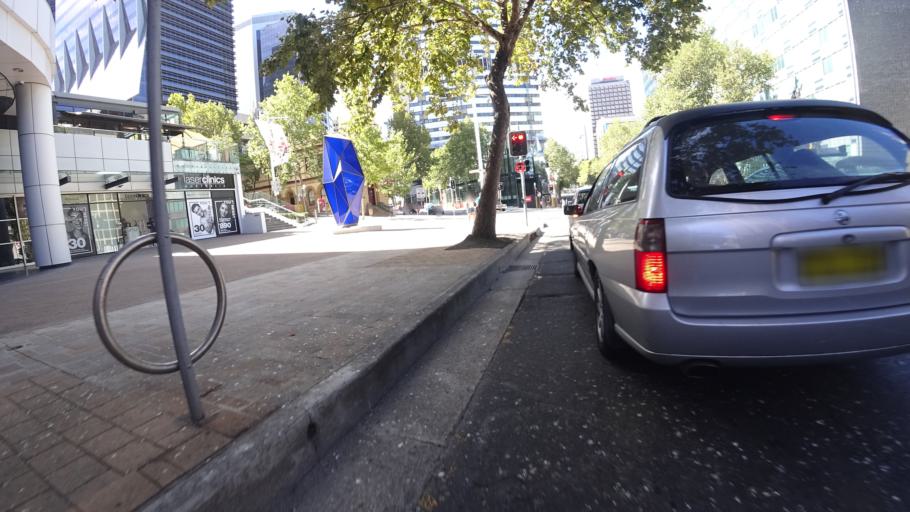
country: AU
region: New South Wales
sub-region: North Sydney
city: North Sydney
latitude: -33.8391
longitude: 151.2068
